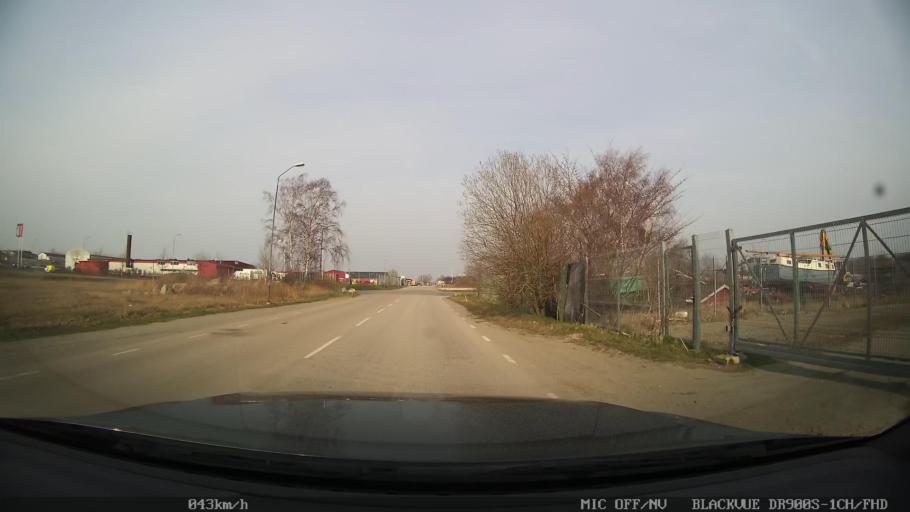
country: SE
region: Skane
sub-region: Ystads Kommun
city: Ystad
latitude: 55.4437
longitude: 13.8478
